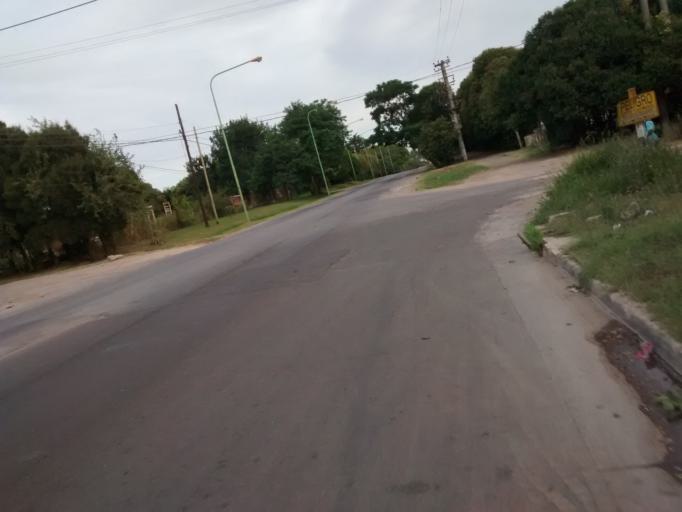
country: AR
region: Buenos Aires
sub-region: Partido de La Plata
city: La Plata
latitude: -34.9078
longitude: -58.0141
